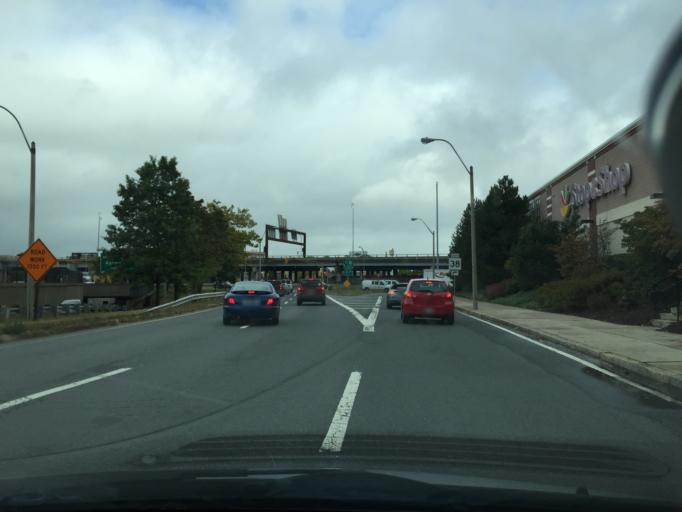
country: US
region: Massachusetts
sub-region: Middlesex County
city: Somerville
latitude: 42.3916
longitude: -71.0860
